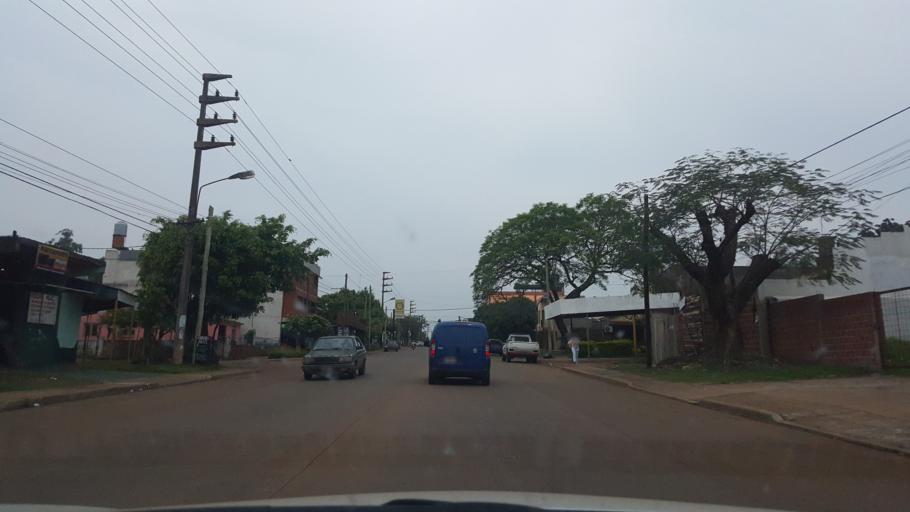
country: AR
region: Misiones
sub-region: Departamento de Capital
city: Posadas
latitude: -27.3884
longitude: -55.9119
